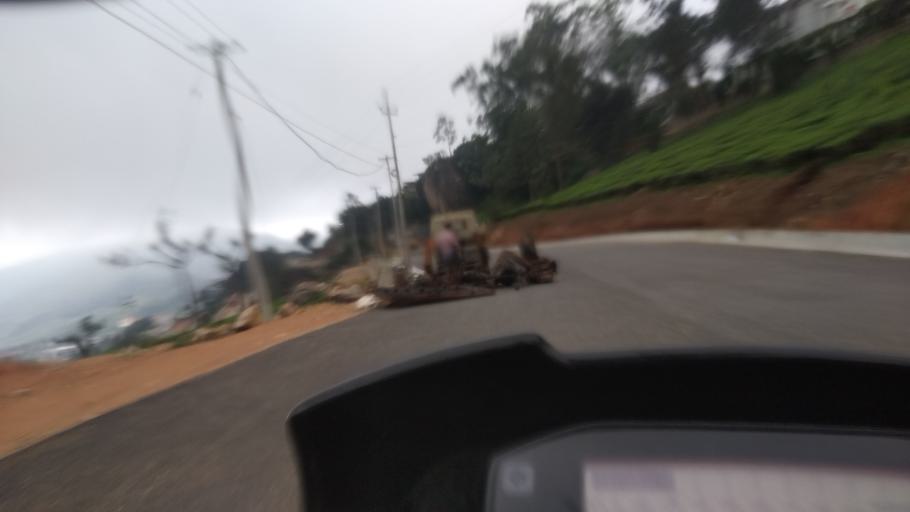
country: IN
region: Kerala
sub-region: Idukki
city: Munnar
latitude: 10.0339
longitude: 77.1600
